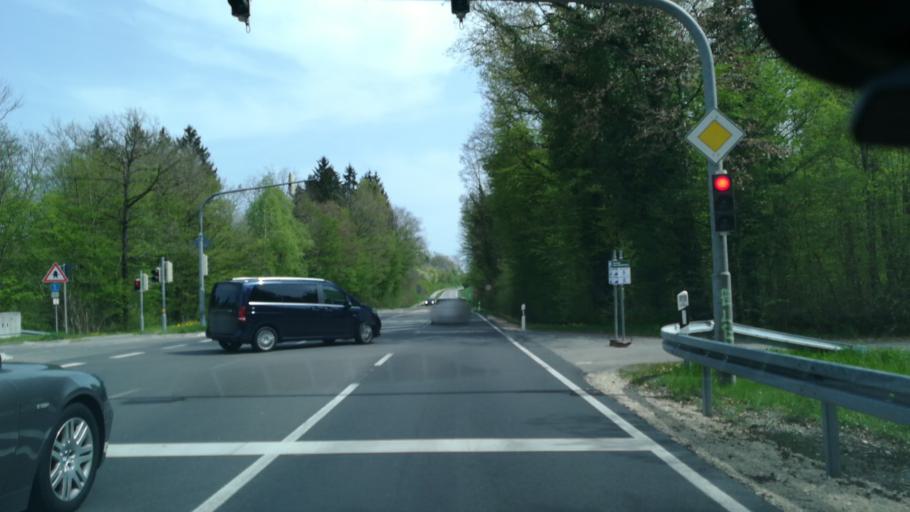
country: DE
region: Baden-Wuerttemberg
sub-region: Freiburg Region
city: Moos
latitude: 47.7581
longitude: 8.9064
